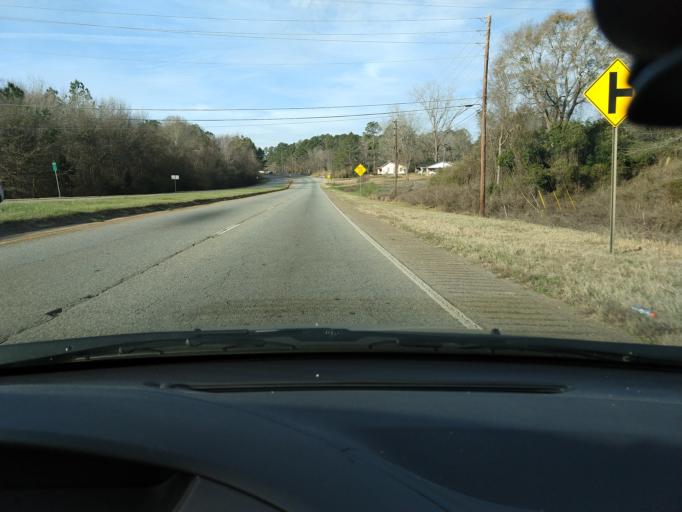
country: US
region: Georgia
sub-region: Sumter County
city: Americus
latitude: 32.0619
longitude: -84.2639
